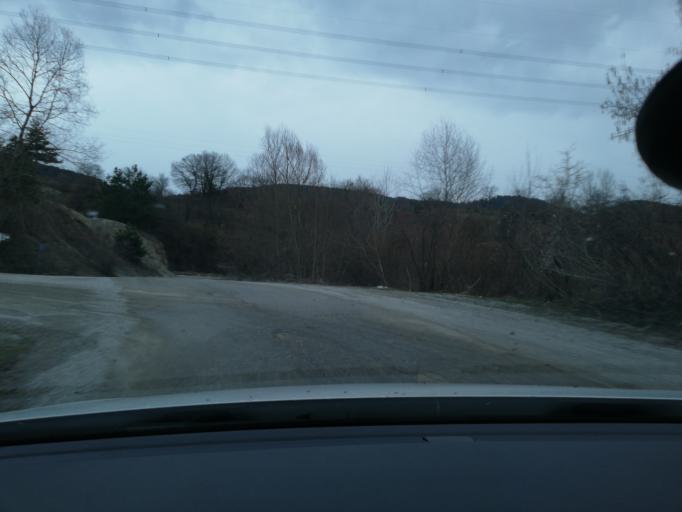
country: TR
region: Bolu
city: Gokcesu
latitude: 40.7389
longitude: 31.8402
